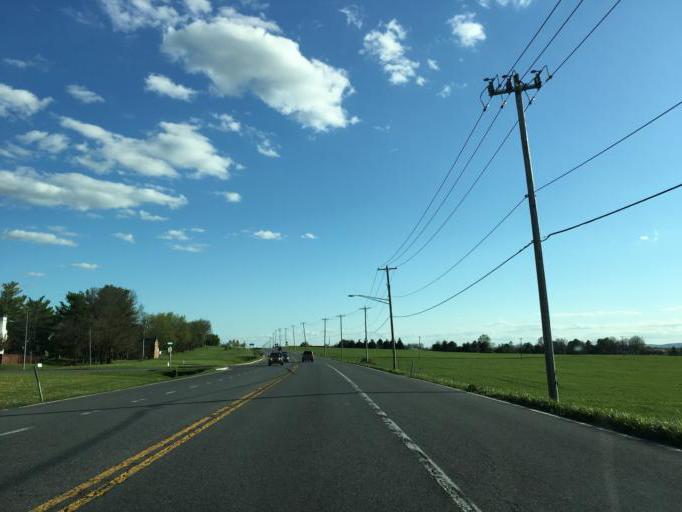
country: US
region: Maryland
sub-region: Frederick County
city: Walkersville
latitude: 39.4694
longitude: -77.3626
